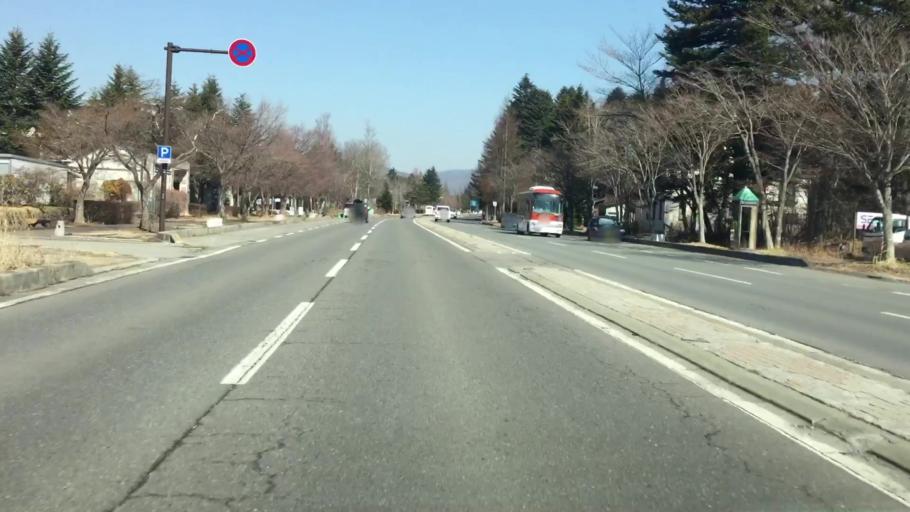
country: JP
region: Nagano
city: Saku
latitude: 36.3336
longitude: 138.6315
